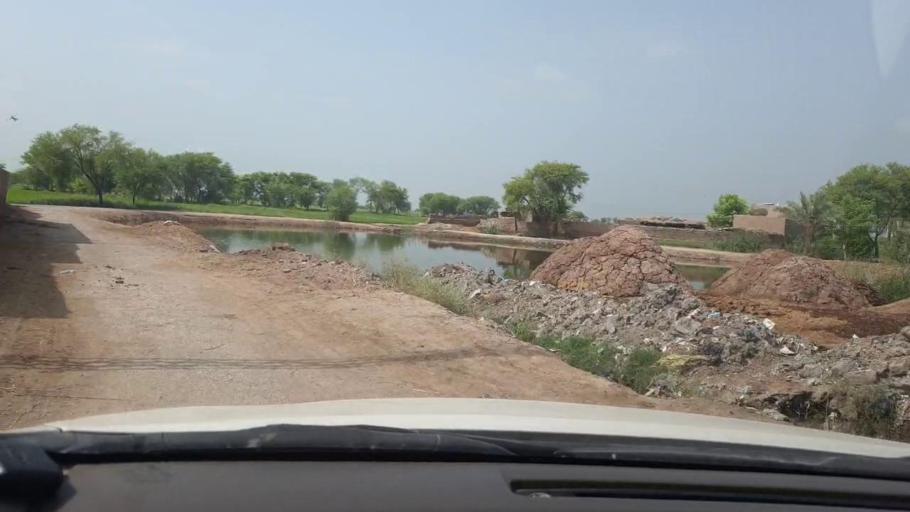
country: PK
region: Sindh
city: Shikarpur
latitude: 27.9916
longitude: 68.5838
